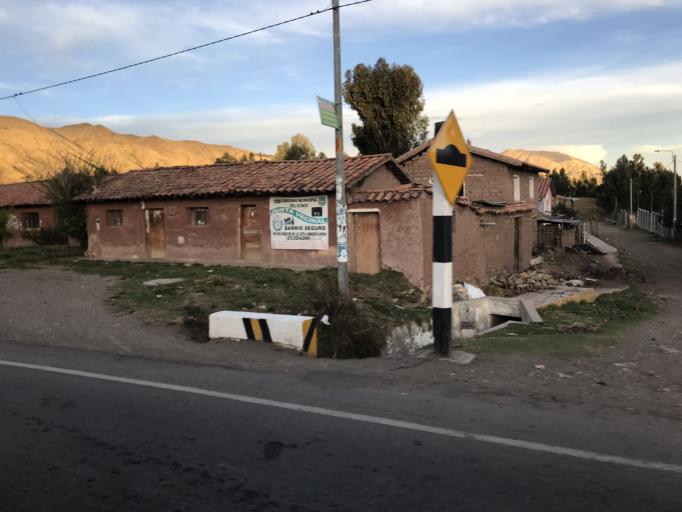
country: PE
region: Cusco
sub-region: Provincia de Cusco
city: Cusco
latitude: -13.4887
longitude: -71.9642
